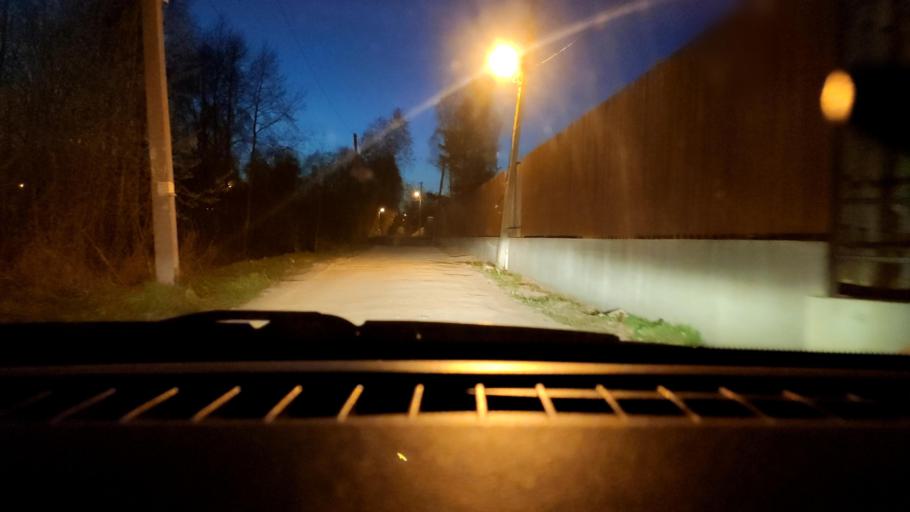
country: RU
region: Perm
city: Perm
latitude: 58.0286
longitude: 56.2055
